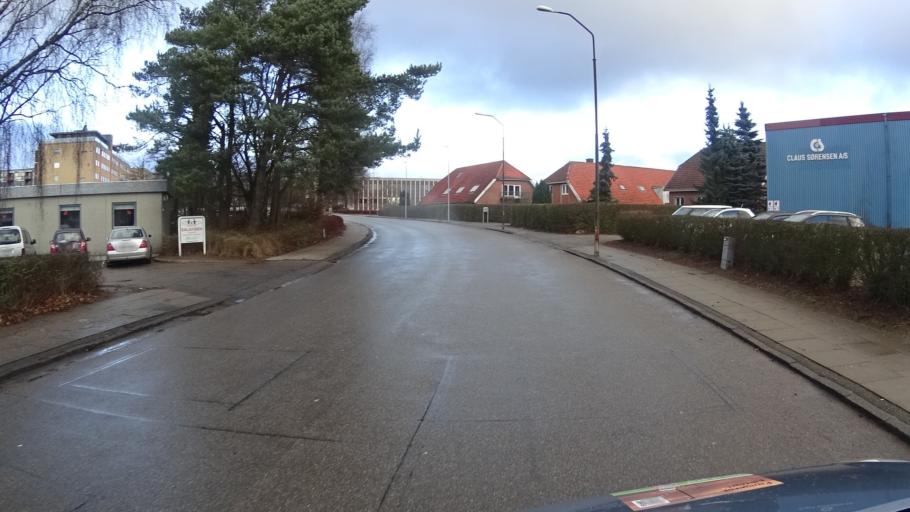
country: DK
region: South Denmark
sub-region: Vejle Kommune
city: Vejle
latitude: 55.7210
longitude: 9.5627
